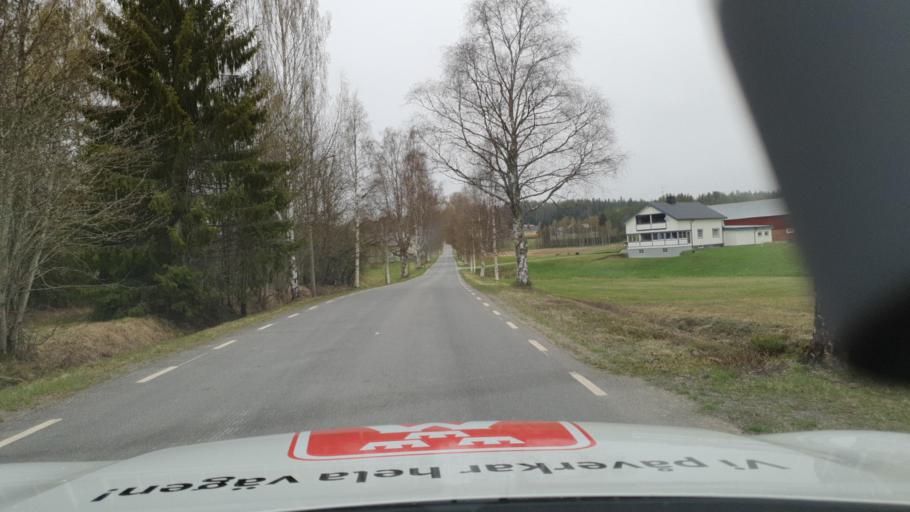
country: SE
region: Vaesterbotten
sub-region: Nordmalings Kommun
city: Nordmaling
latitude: 63.7245
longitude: 19.5143
